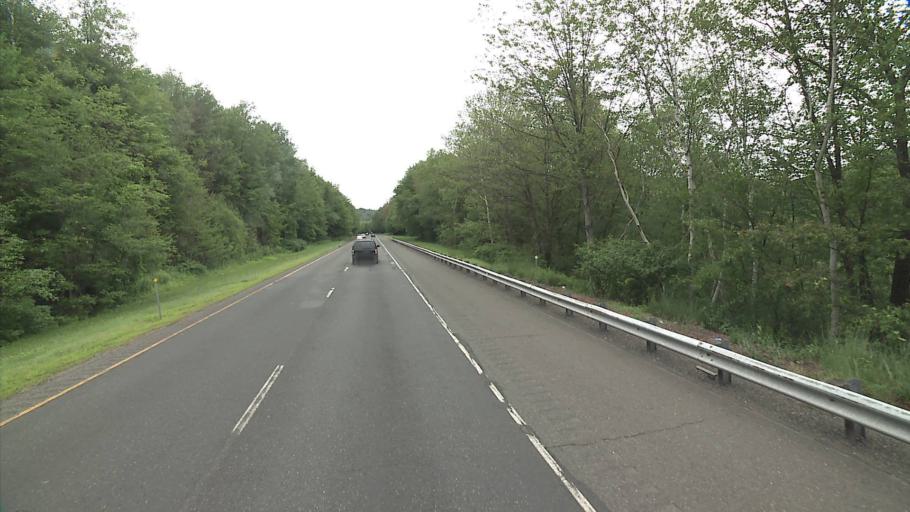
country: US
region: Connecticut
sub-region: Litchfield County
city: Oakville
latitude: 41.6231
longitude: -73.0677
